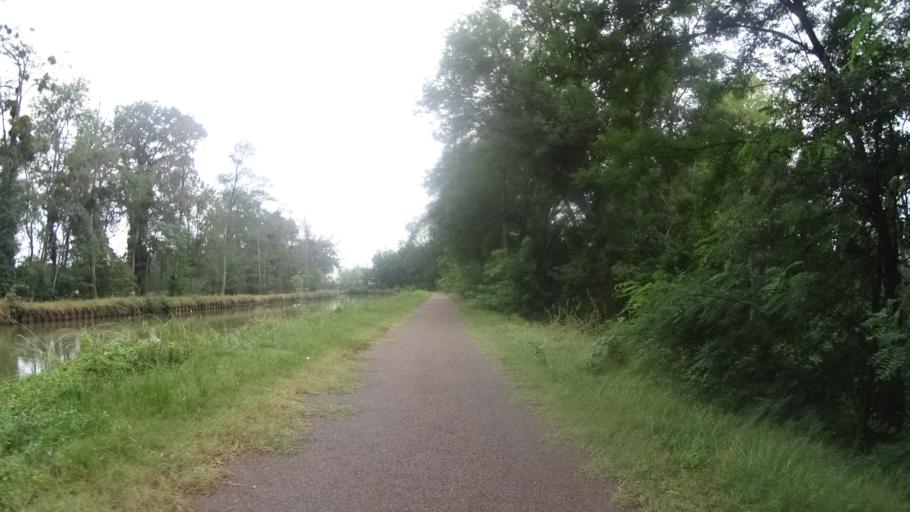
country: FR
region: Bourgogne
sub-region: Departement de la Nievre
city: Saint-Leger-des-Vignes
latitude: 46.8207
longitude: 3.4094
